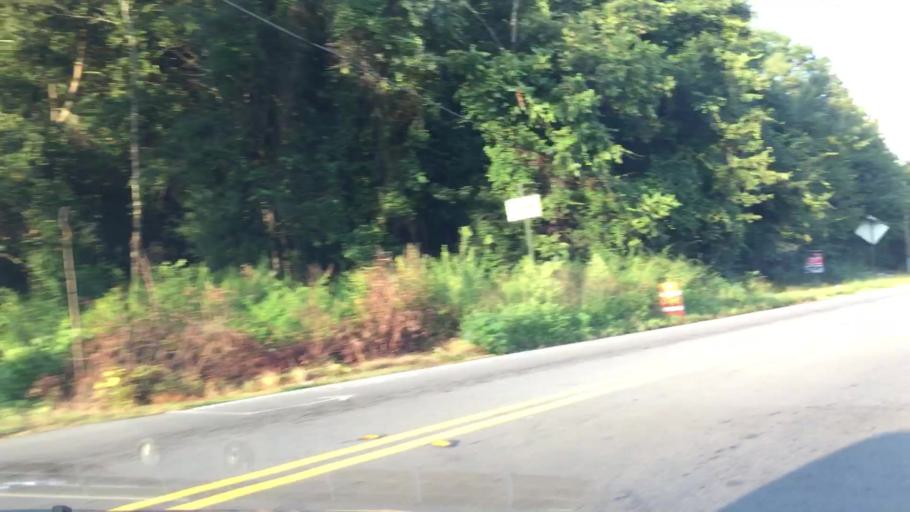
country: US
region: Georgia
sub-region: Henry County
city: McDonough
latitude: 33.4832
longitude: -84.1945
